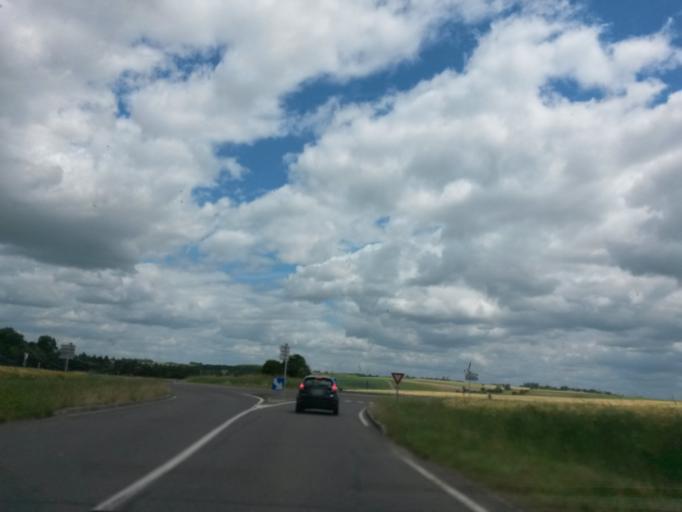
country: FR
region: Bourgogne
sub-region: Departement de la Nievre
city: Cosne-Cours-sur-Loire
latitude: 47.3853
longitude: 2.9442
